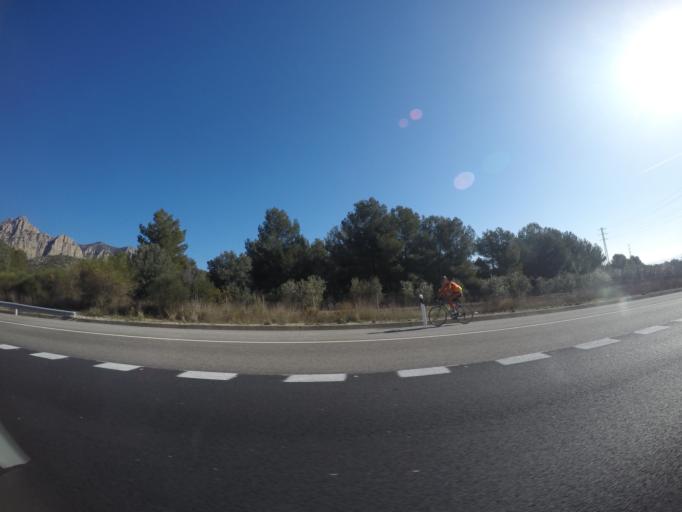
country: ES
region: Catalonia
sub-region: Provincia de Barcelona
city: Collbato
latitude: 41.5590
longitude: 1.8344
